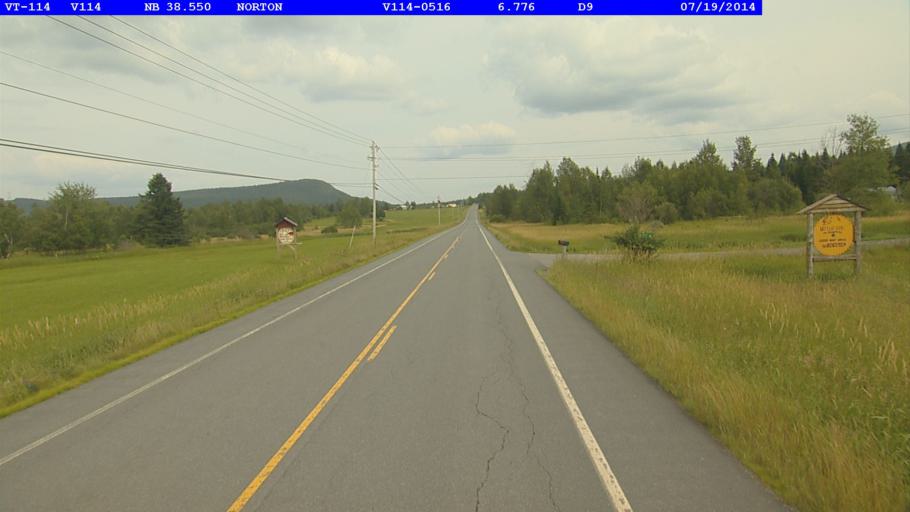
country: CA
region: Quebec
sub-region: Estrie
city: Coaticook
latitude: 45.0051
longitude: -71.7680
